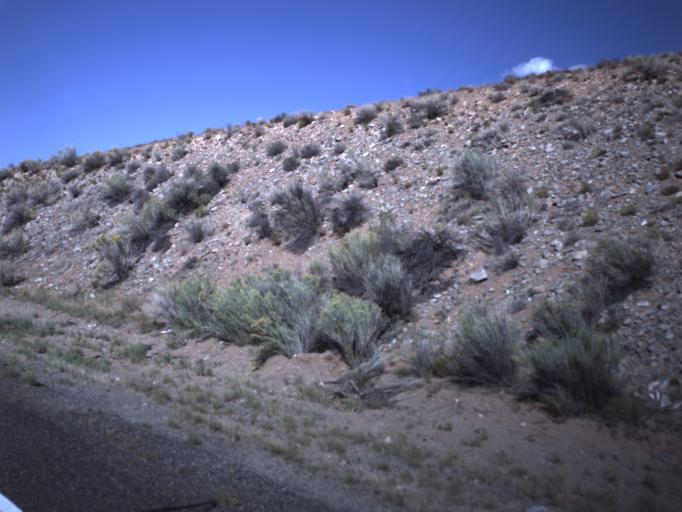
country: US
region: Utah
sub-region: Wayne County
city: Loa
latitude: 38.1151
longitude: -110.6239
